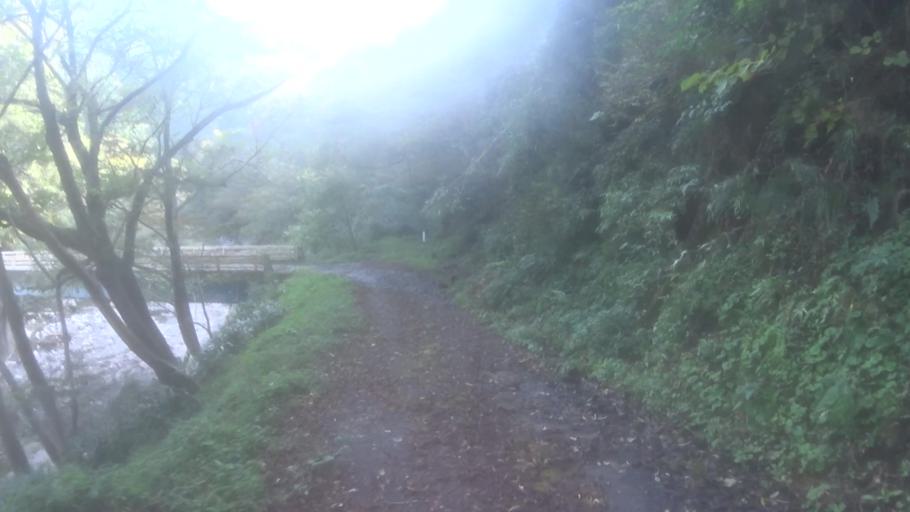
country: JP
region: Kyoto
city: Miyazu
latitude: 35.7164
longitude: 135.1643
